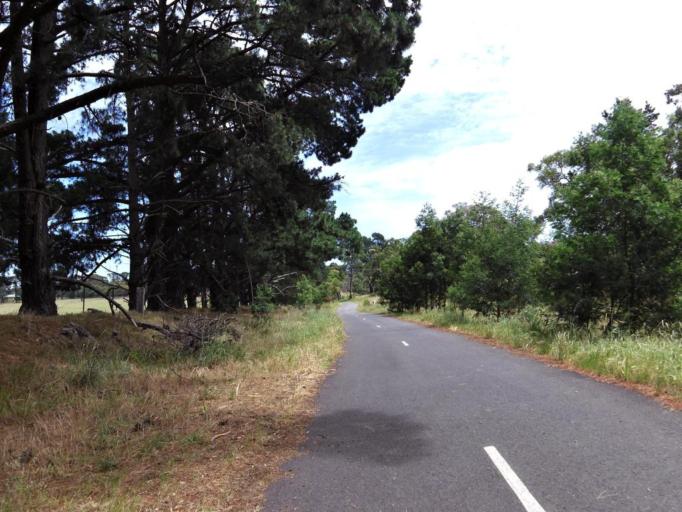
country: AU
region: Victoria
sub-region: Mornington Peninsula
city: Moorooduc
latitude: -38.2118
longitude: 145.1206
